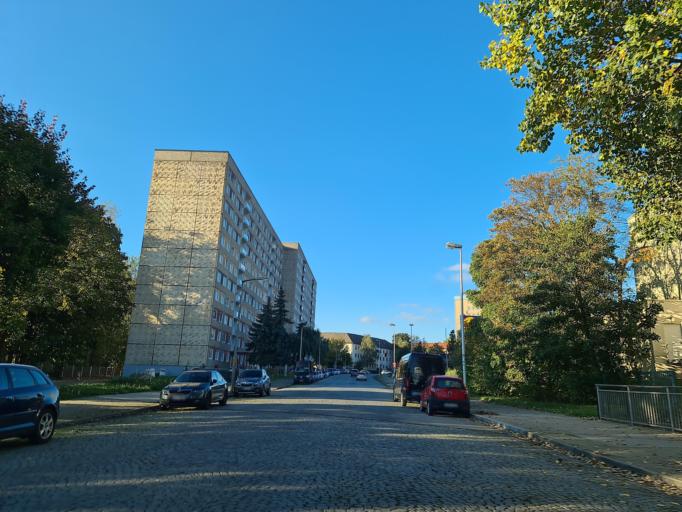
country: DE
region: Thuringia
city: Gera
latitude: 50.8923
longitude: 12.0830
